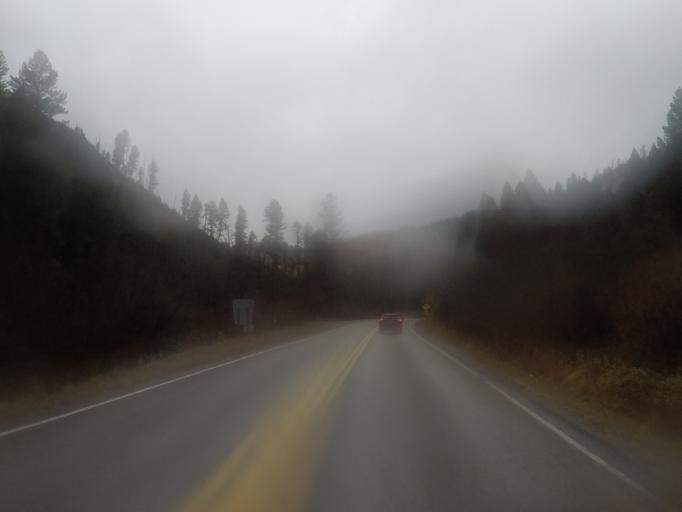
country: US
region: Montana
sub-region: Broadwater County
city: Townsend
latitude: 46.3320
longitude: -111.2106
